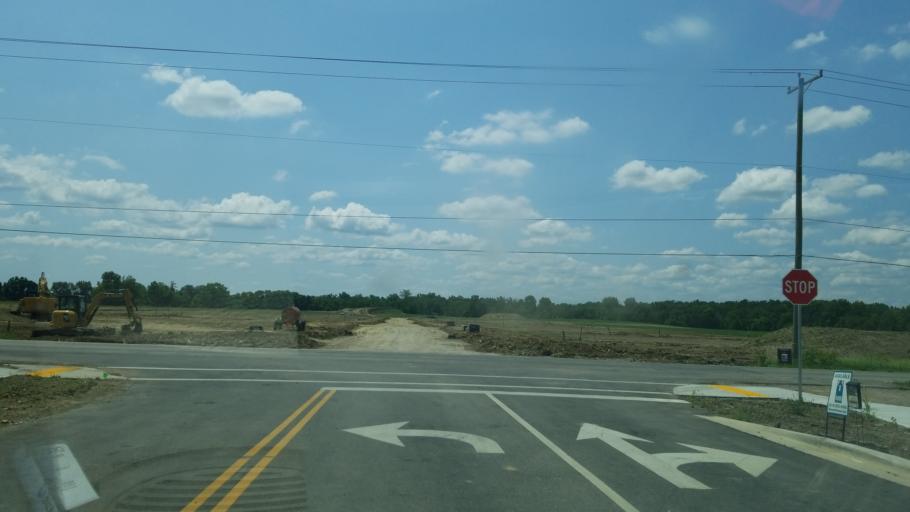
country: US
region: Ohio
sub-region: Delaware County
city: Lewis Center
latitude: 40.2400
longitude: -82.9980
